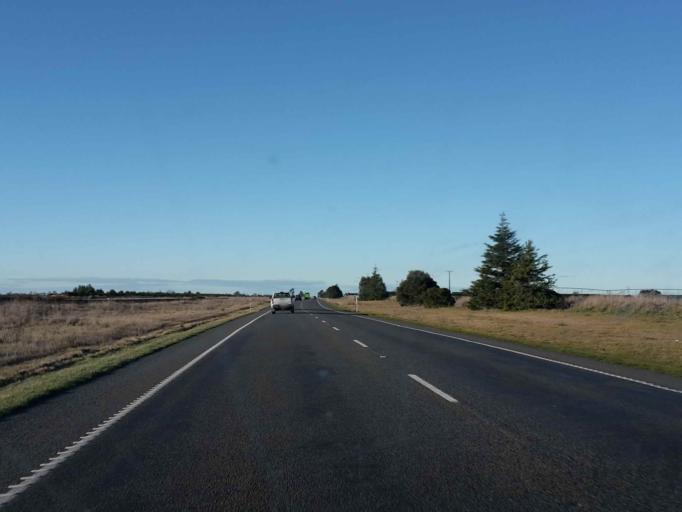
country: NZ
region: Canterbury
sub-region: Ashburton District
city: Tinwald
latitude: -44.0324
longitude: 171.4682
